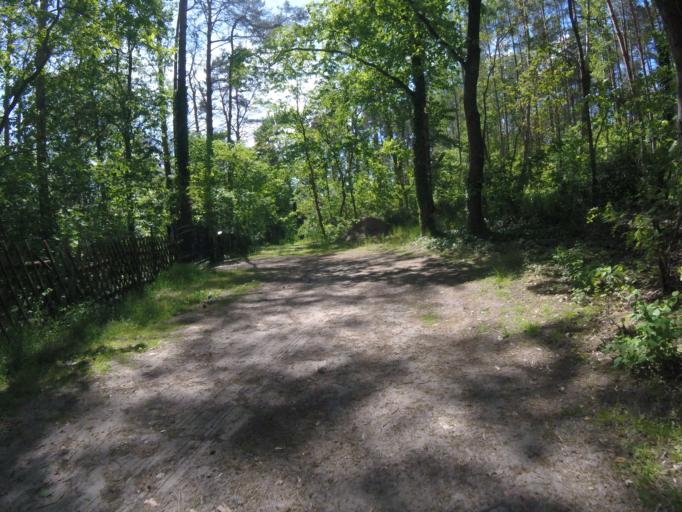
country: DE
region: Brandenburg
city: Teupitz
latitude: 52.1453
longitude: 13.5956
